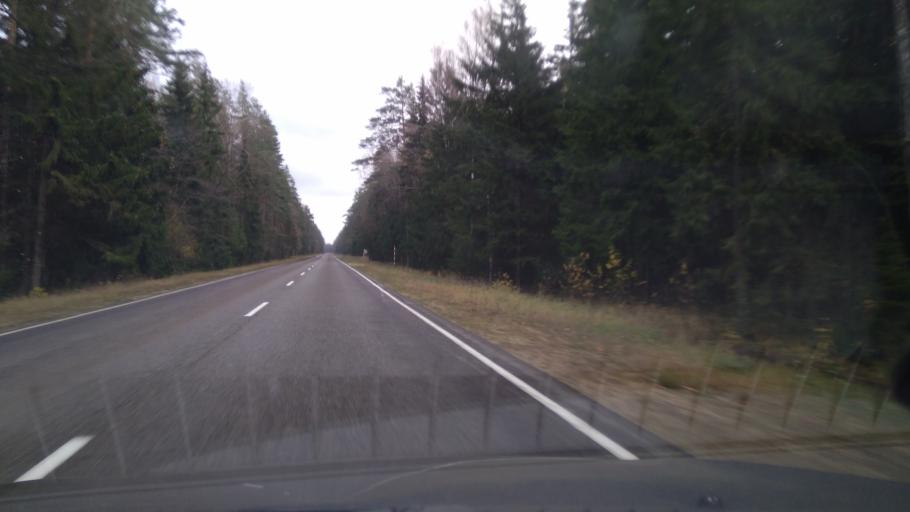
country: BY
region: Minsk
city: Urechcha
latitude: 53.2094
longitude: 27.8119
